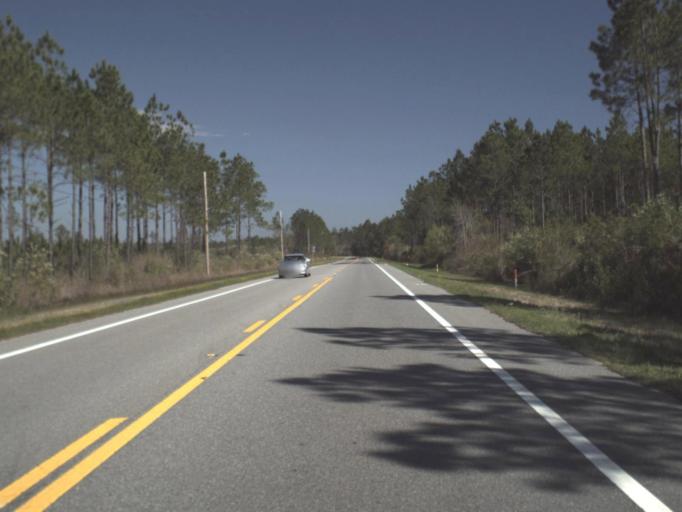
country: US
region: Florida
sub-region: Bay County
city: Lynn Haven
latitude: 30.3300
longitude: -85.7460
